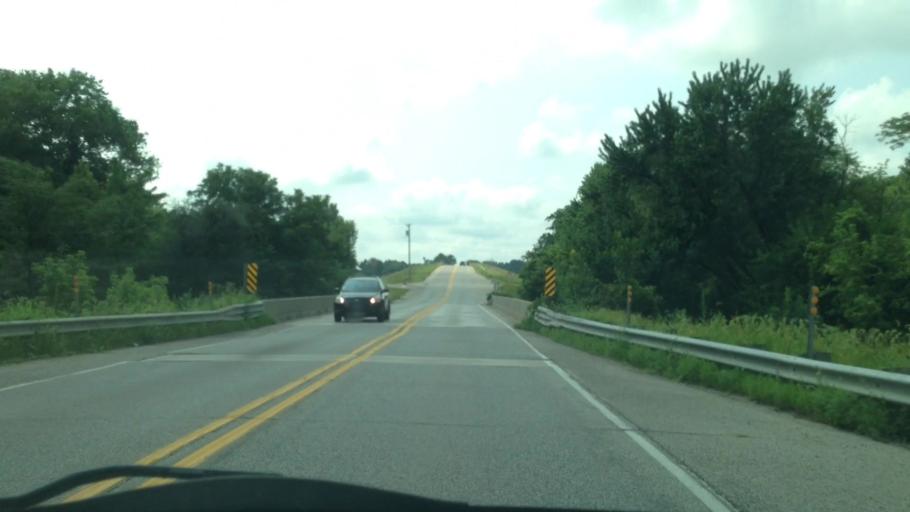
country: US
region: Iowa
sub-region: Linn County
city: Fairfax
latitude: 41.9237
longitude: -91.7839
